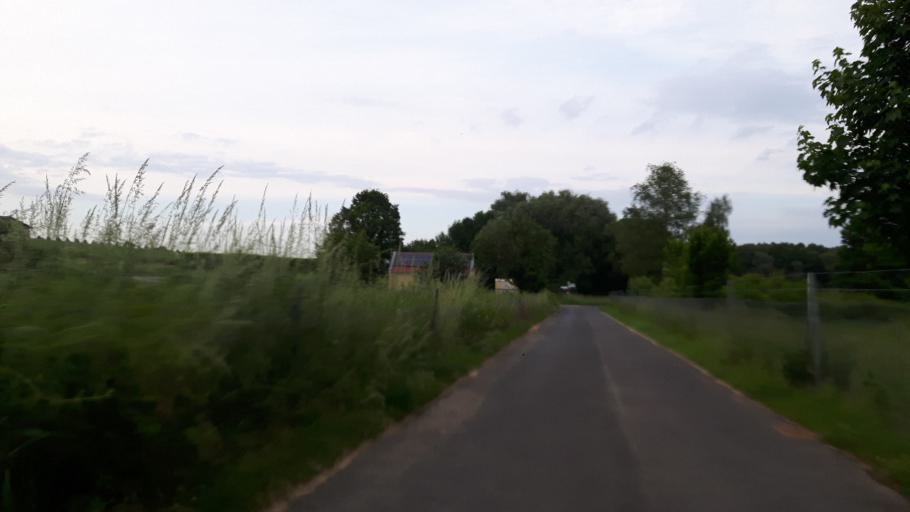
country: DE
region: Bavaria
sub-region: Regierungsbezirk Unterfranken
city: Estenfeld
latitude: 49.8139
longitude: 9.9898
